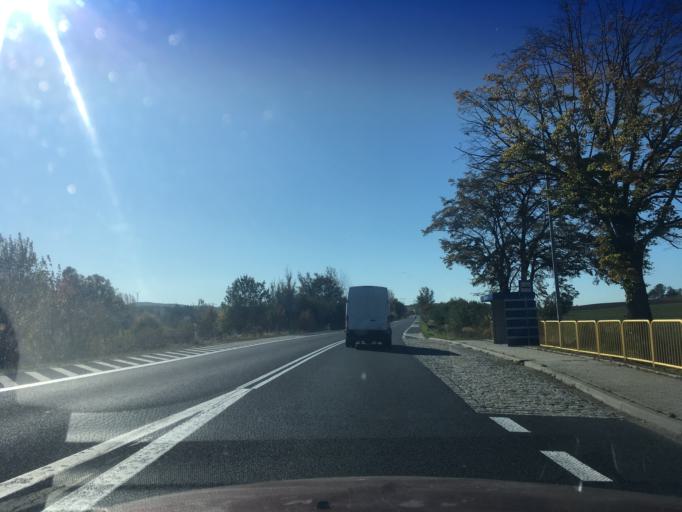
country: DE
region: Saxony
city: Ostritz
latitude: 51.0334
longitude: 14.9719
